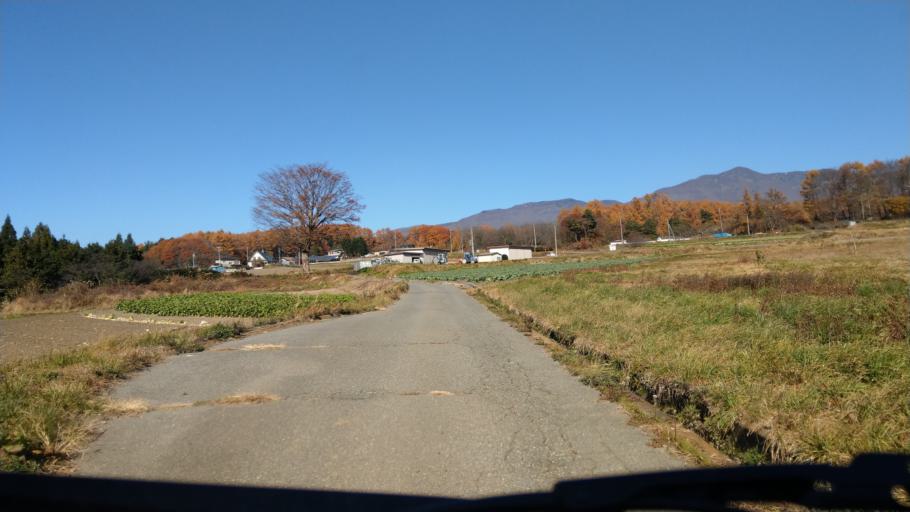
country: JP
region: Nagano
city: Komoro
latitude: 36.3367
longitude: 138.4580
